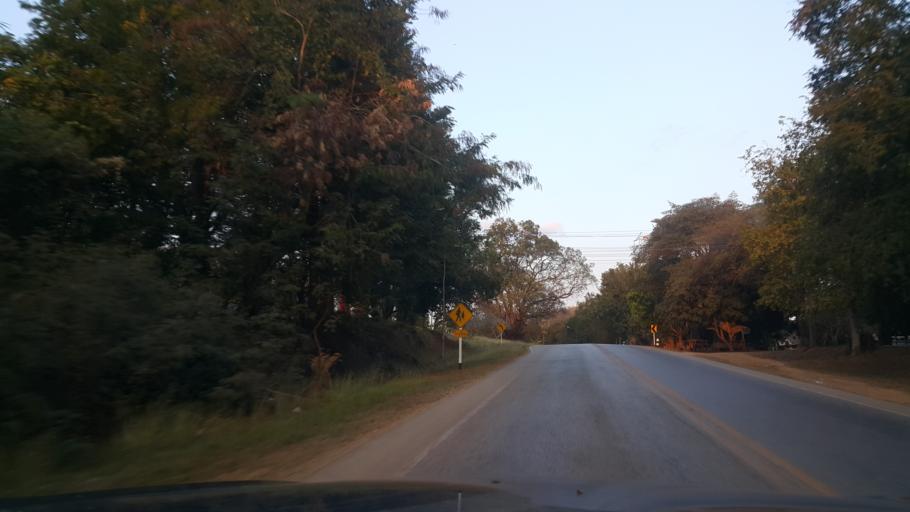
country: TH
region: Loei
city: Loei
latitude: 17.4764
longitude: 101.6025
